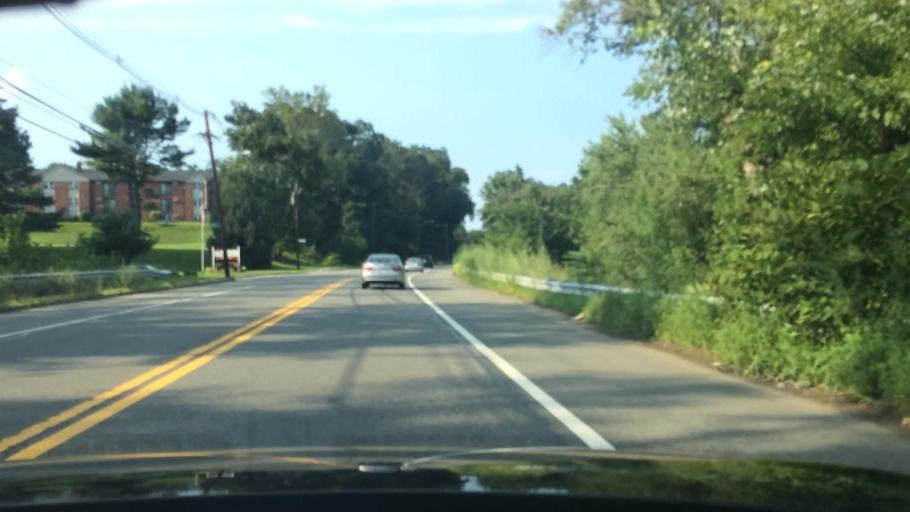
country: US
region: Massachusetts
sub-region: Essex County
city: Haverhill
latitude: 42.7619
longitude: -71.1318
